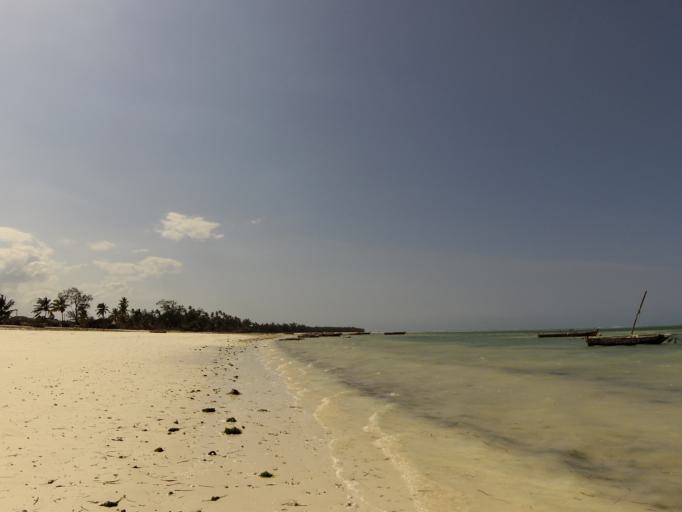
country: TZ
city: Kiwengwa
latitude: -6.0937
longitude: 39.4261
